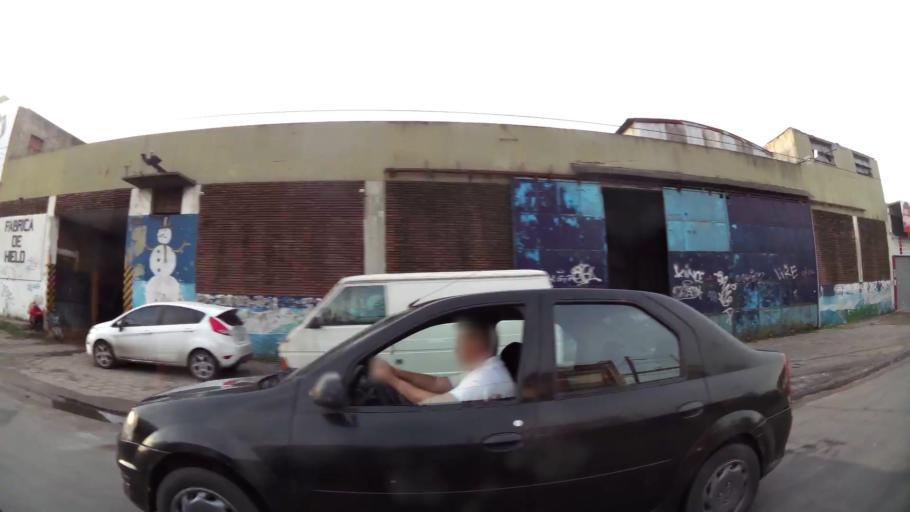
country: AR
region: Buenos Aires
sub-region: Partido de Lomas de Zamora
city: Lomas de Zamora
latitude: -34.7671
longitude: -58.3729
